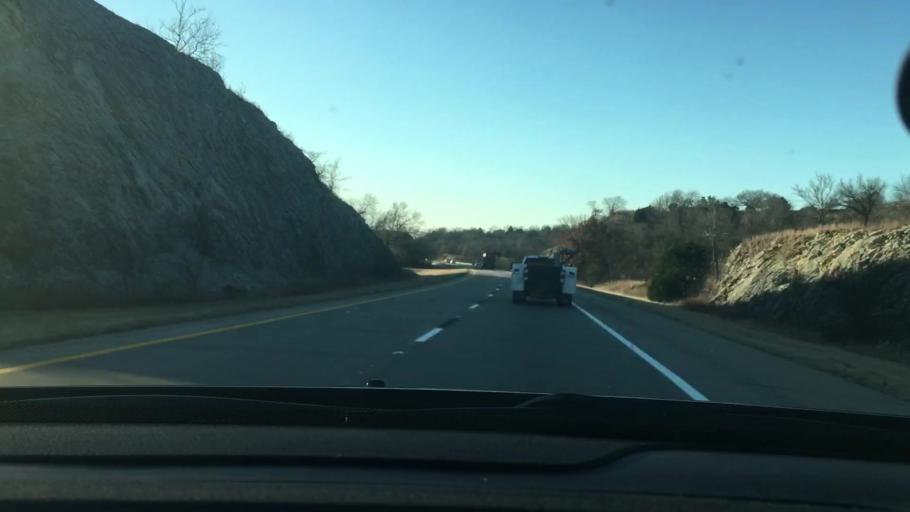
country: US
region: Oklahoma
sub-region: Murray County
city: Davis
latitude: 34.3584
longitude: -97.1490
